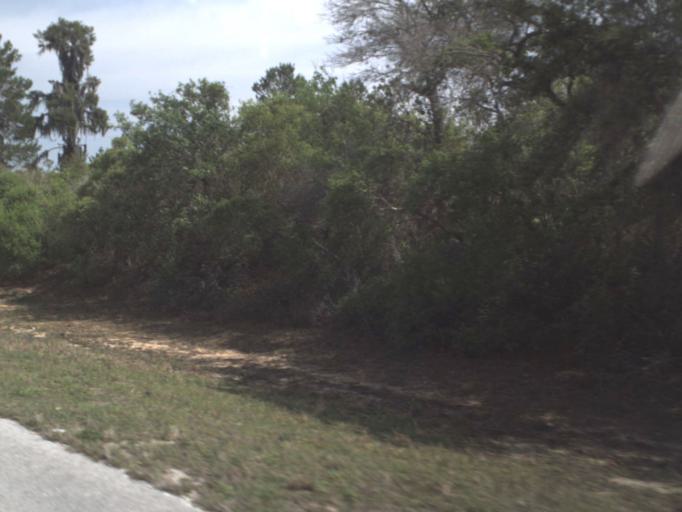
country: US
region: Florida
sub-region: Lake County
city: Astor
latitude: 29.2381
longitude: -81.6464
